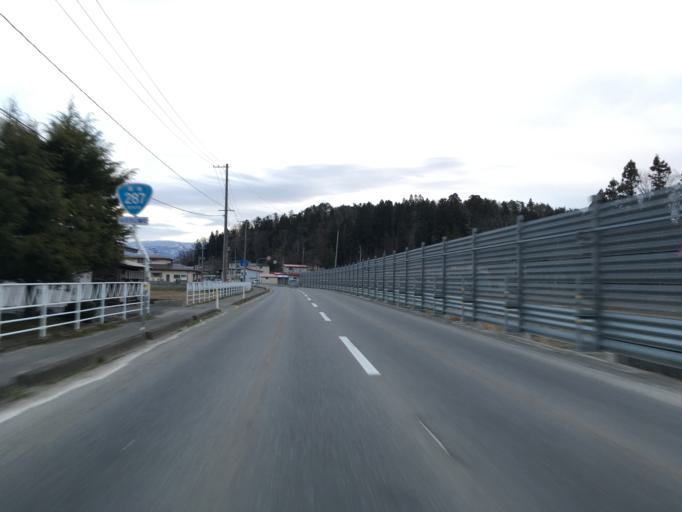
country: JP
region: Yamagata
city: Yonezawa
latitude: 37.9469
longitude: 140.0726
